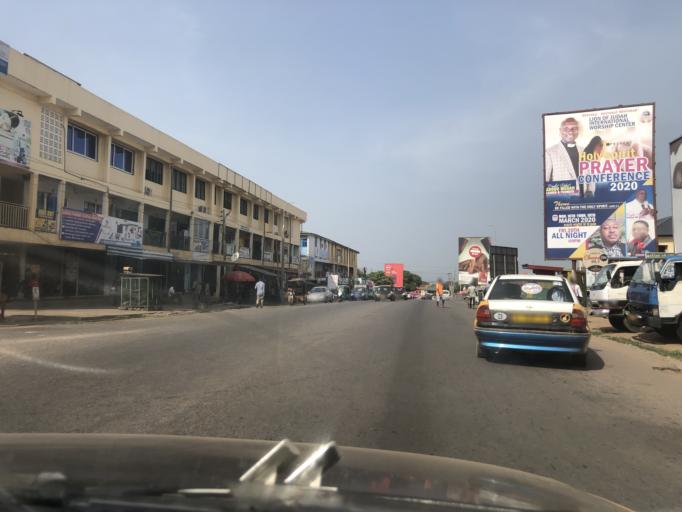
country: GH
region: Eastern
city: Koforidua
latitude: 6.0965
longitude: -0.2557
